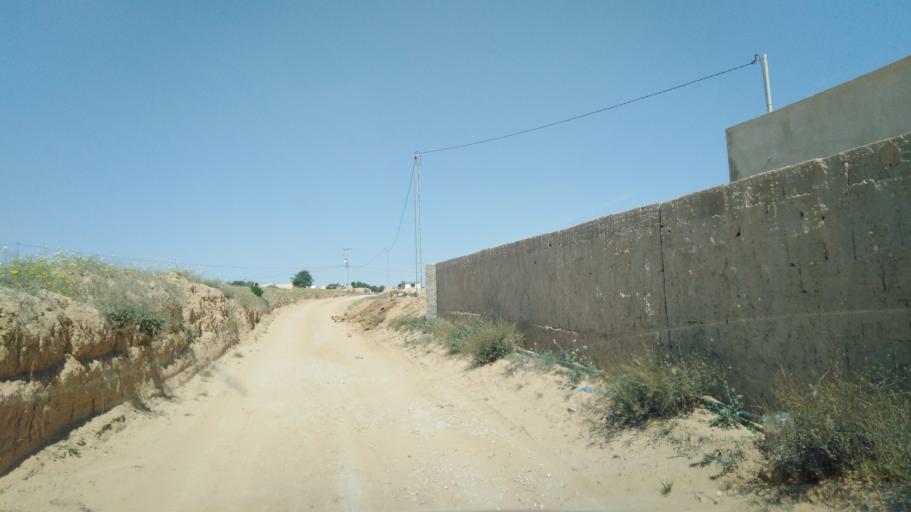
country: TN
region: Safaqis
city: Sfax
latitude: 34.7773
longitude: 10.5256
